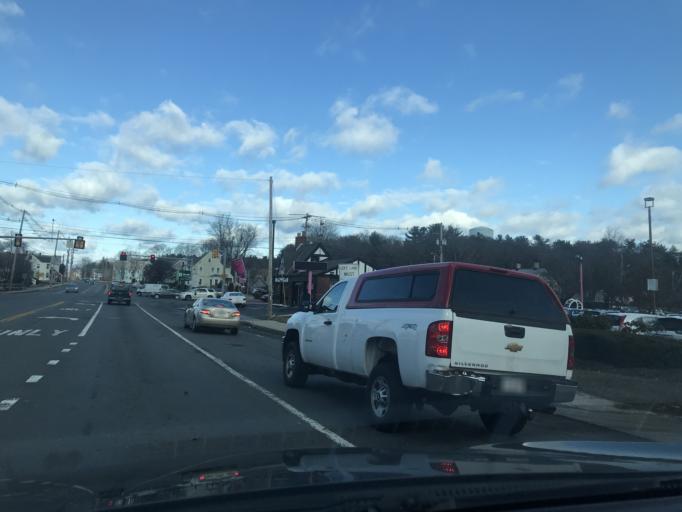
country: US
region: Massachusetts
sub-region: Norfolk County
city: Weymouth
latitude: 42.1789
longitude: -70.9553
